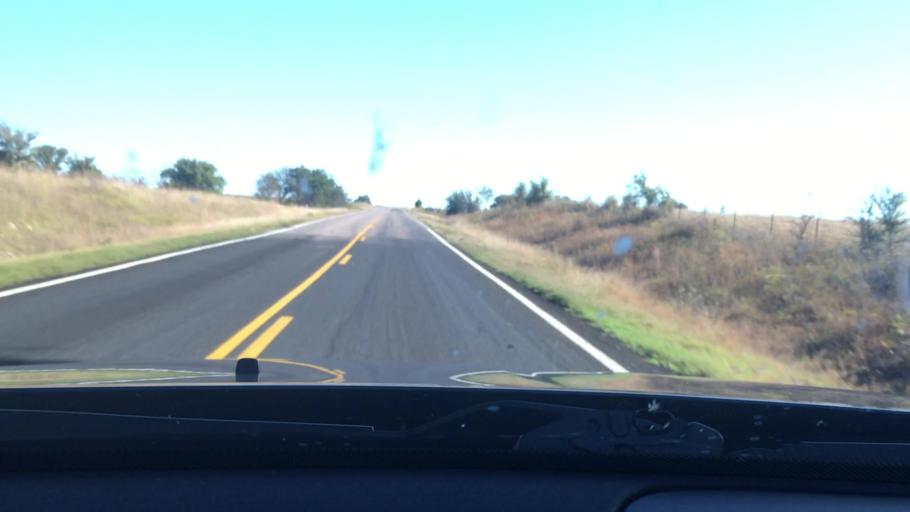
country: US
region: Oklahoma
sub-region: Marshall County
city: Madill
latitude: 34.1040
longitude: -96.7515
